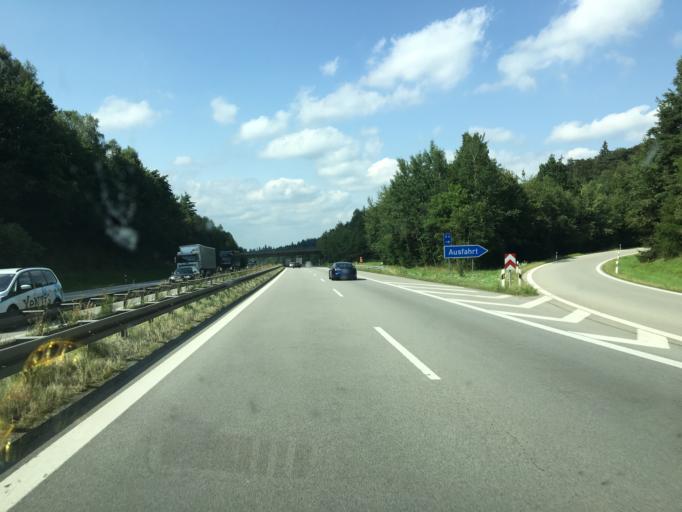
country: DE
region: Bavaria
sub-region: Lower Bavaria
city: Passau
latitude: 48.5336
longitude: 13.4001
